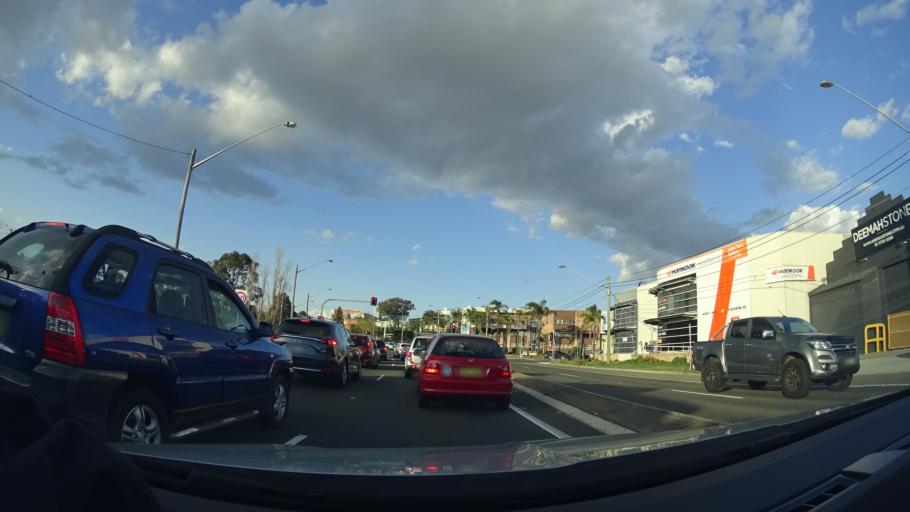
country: AU
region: New South Wales
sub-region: Canterbury
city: Lakemba
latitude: -33.9100
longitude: 151.0749
